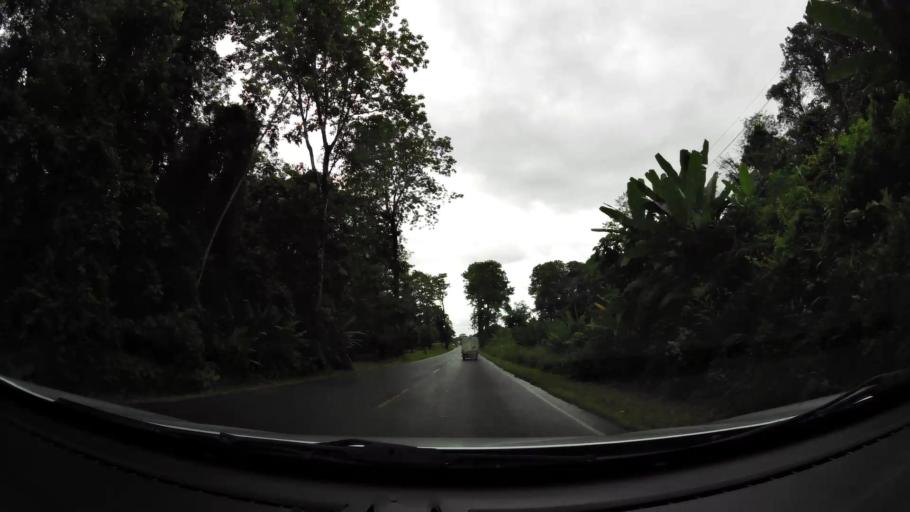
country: CR
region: Limon
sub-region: Canton de Siquirres
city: Siquirres
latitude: 10.1223
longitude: -83.5538
